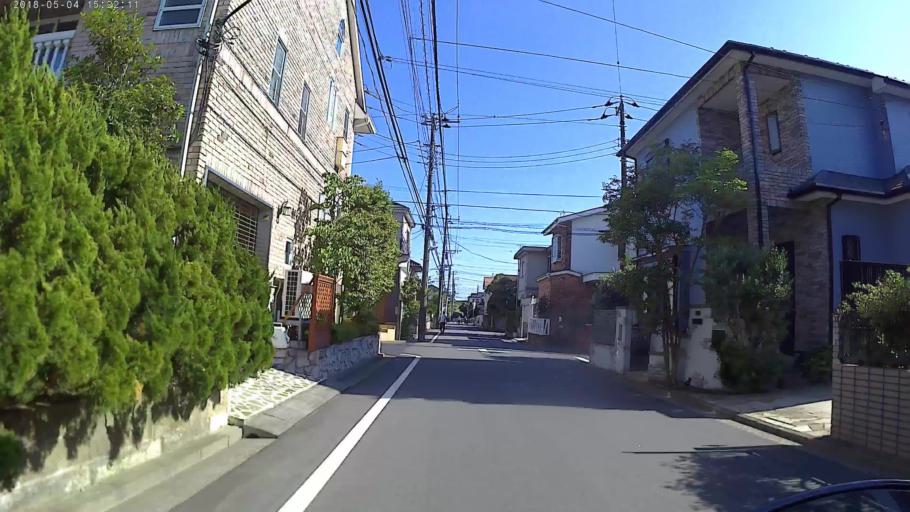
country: JP
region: Kanagawa
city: Yokohama
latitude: 35.5371
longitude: 139.6198
